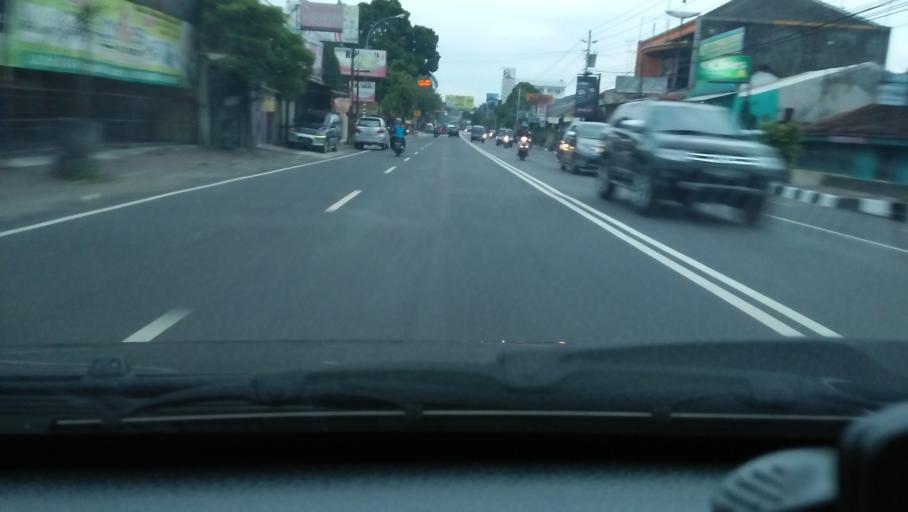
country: ID
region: Central Java
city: Magelang
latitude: -7.4503
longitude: 110.2243
